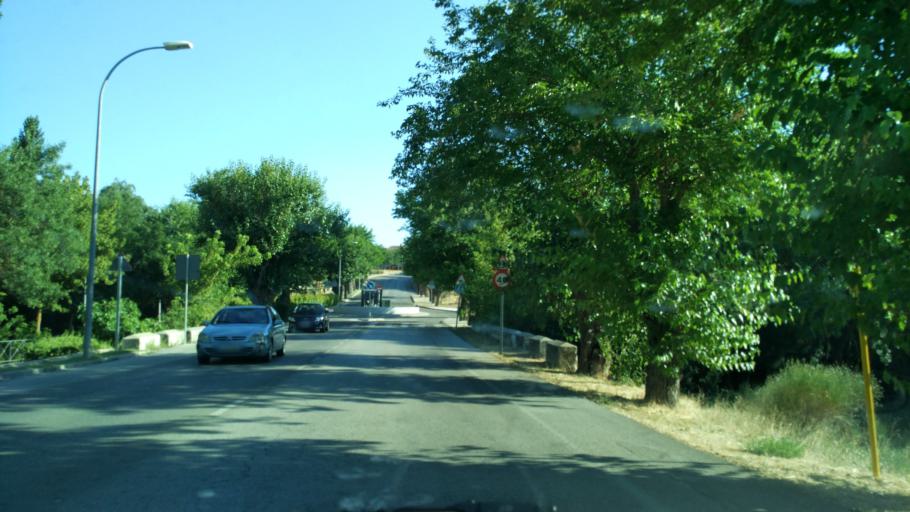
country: ES
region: Madrid
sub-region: Provincia de Madrid
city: San Agustin de Guadalix
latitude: 40.6864
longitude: -3.6109
